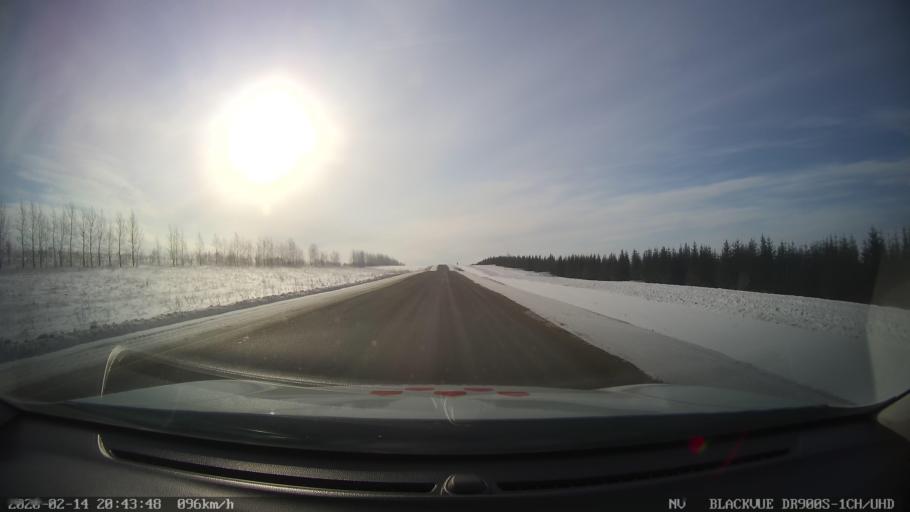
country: RU
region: Tatarstan
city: Kuybyshevskiy Zaton
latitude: 55.3035
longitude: 49.1478
